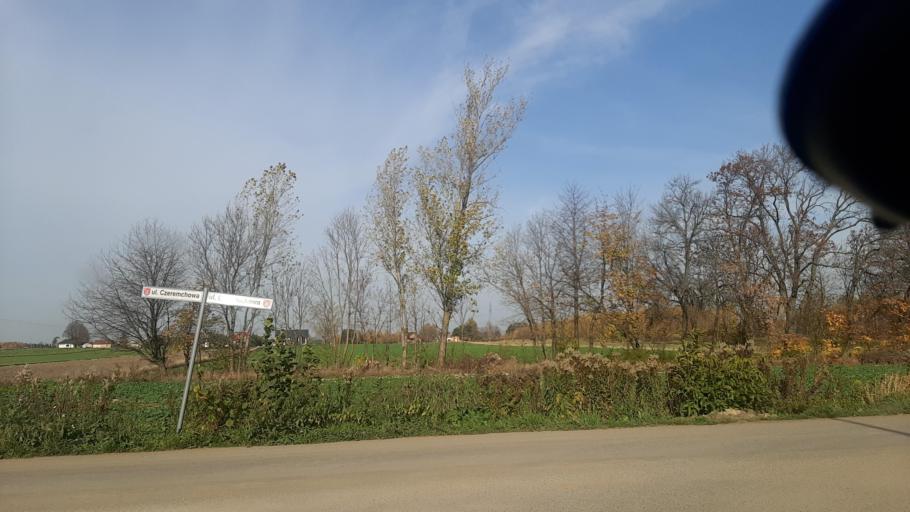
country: PL
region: Lublin Voivodeship
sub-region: Powiat lubelski
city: Lublin
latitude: 51.3278
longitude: 22.5384
